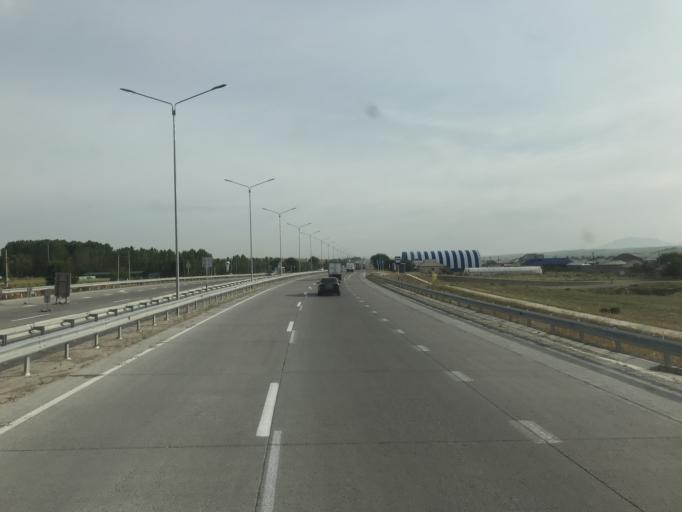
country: KZ
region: Ongtustik Qazaqstan
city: Qazyqurt
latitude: 41.7924
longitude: 69.3925
